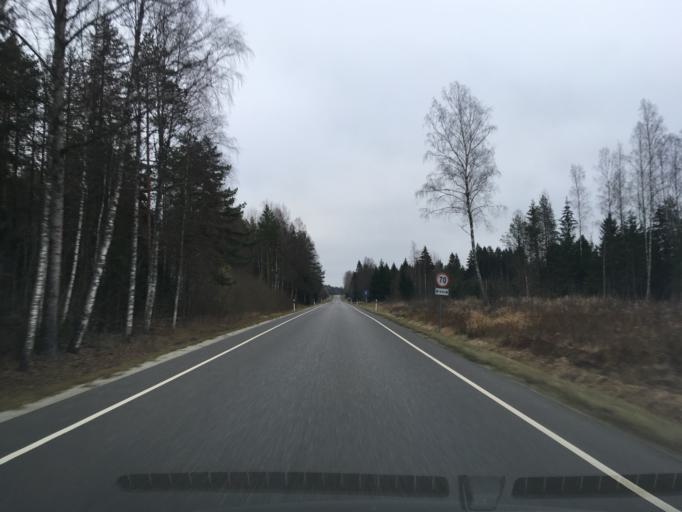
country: EE
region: Laeaene-Virumaa
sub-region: Tapa vald
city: Tapa
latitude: 59.4571
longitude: 25.9740
